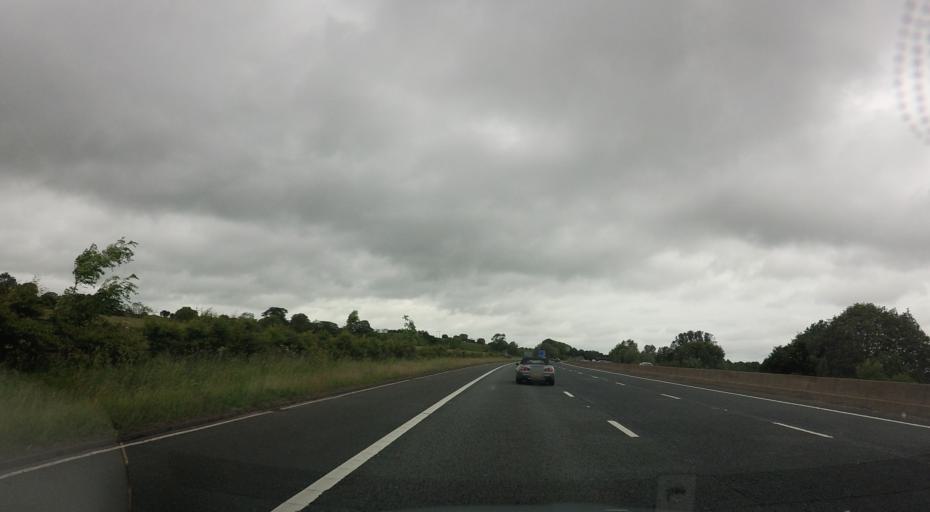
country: GB
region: England
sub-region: Cumbria
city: Penrith
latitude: 54.6854
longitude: -2.7900
